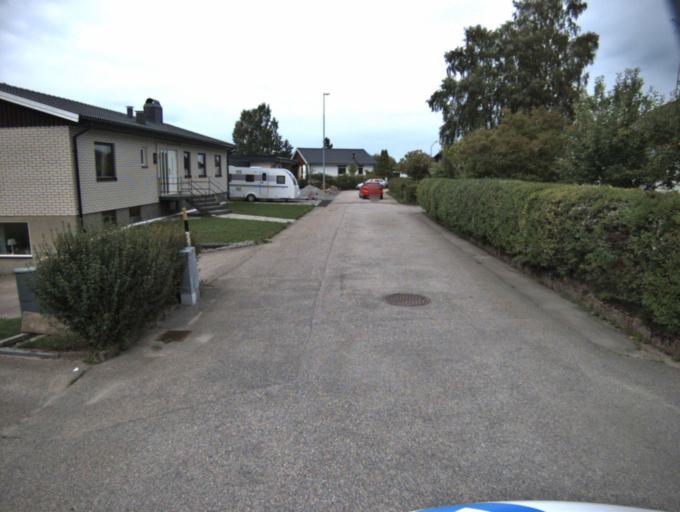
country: SE
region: Vaestra Goetaland
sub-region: Ulricehamns Kommun
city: Ulricehamn
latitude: 57.8384
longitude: 13.2879
